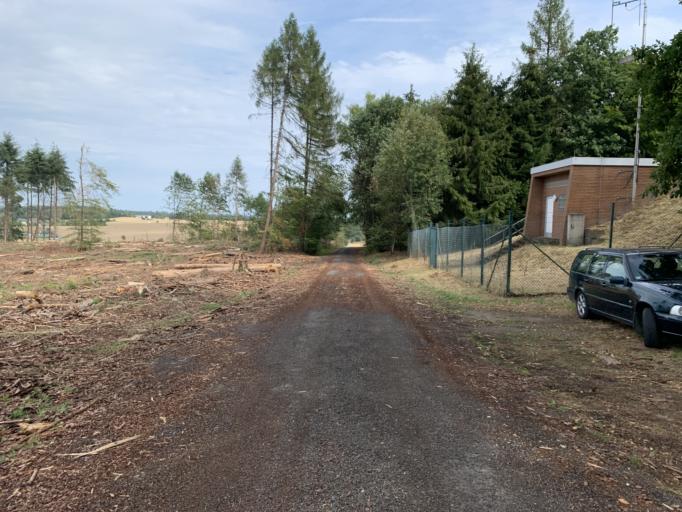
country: DE
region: Rheinland-Pfalz
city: Rettert
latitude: 50.2240
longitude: 7.9469
